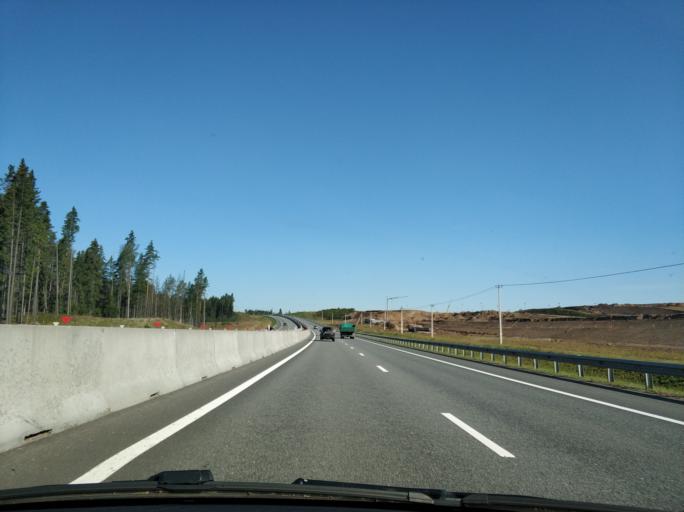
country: RU
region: Leningrad
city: Sosnovo
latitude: 60.5081
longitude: 30.1914
